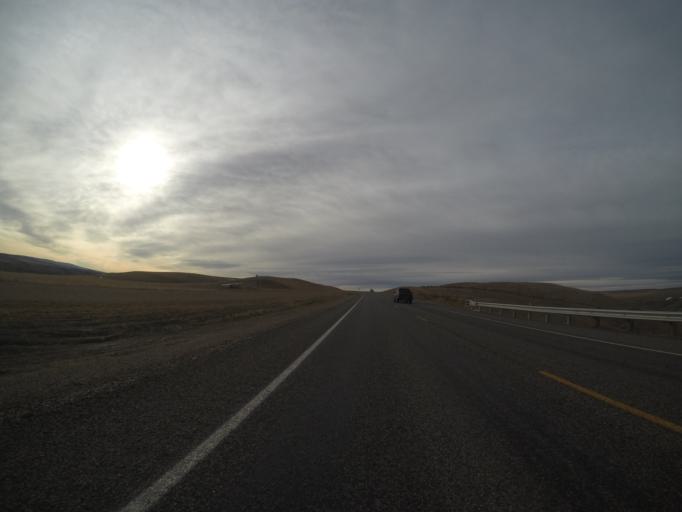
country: US
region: Montana
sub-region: Yellowstone County
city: Laurel
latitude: 45.5699
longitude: -108.8494
